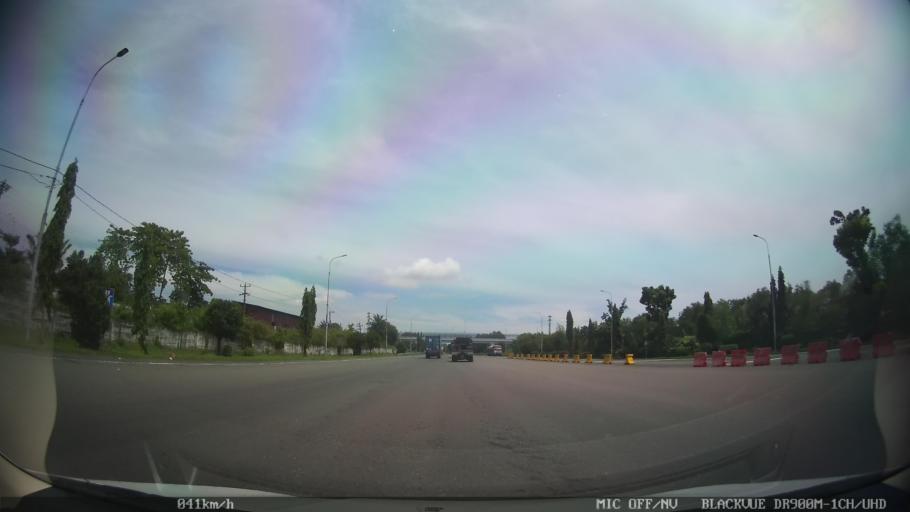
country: ID
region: North Sumatra
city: Labuhan Deli
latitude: 3.7308
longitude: 98.6807
